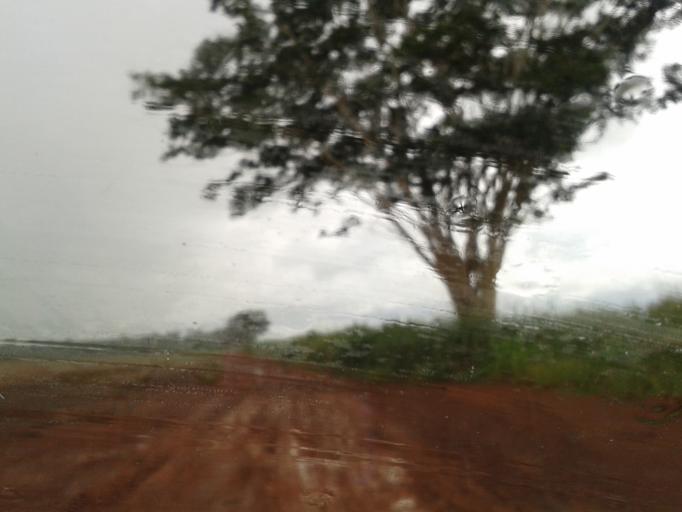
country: BR
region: Minas Gerais
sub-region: Santa Vitoria
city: Santa Vitoria
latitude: -18.6556
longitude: -49.9118
